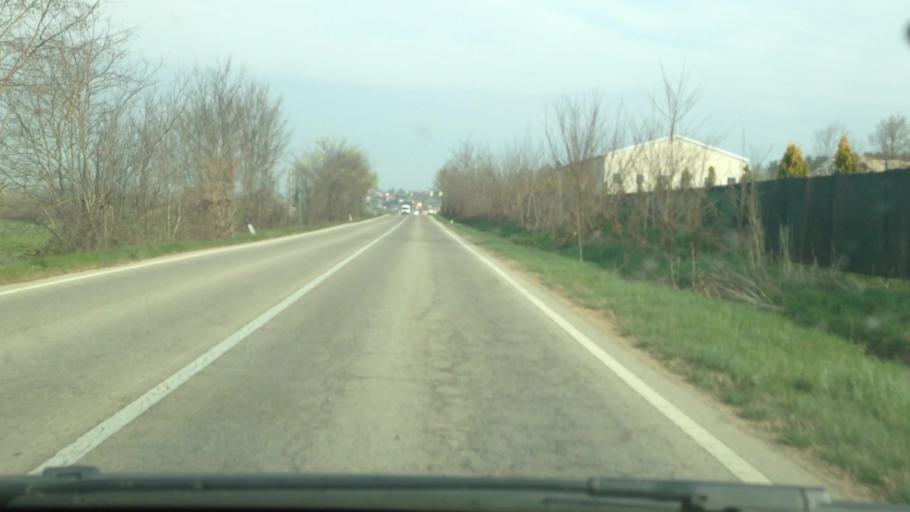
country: IT
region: Piedmont
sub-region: Provincia di Torino
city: Pralormo
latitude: 44.8435
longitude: 7.9105
